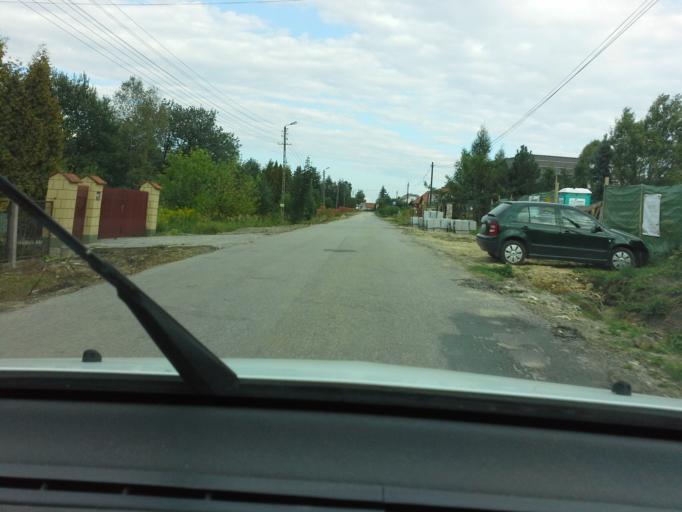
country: PL
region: Lesser Poland Voivodeship
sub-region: Powiat chrzanowski
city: Trzebinia
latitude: 50.1324
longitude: 19.4505
